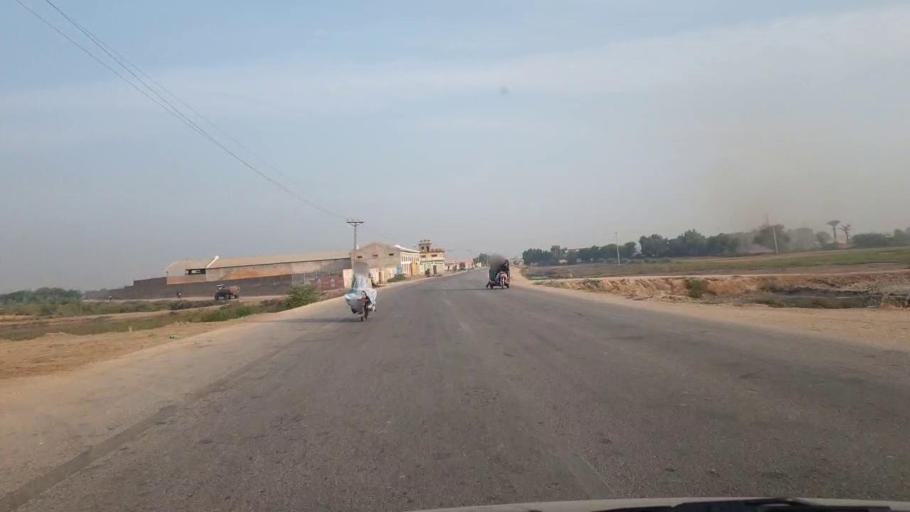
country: PK
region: Sindh
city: Badin
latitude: 24.6849
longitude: 68.8242
